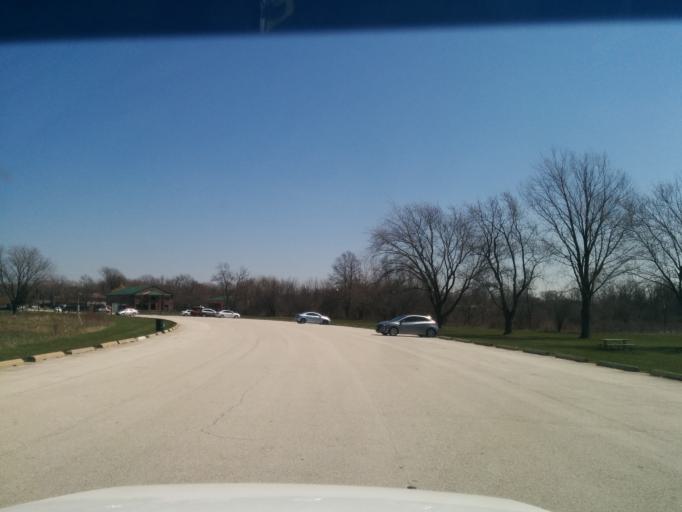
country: US
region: Illinois
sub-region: Cook County
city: Midlothian
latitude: 41.6077
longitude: -87.7195
